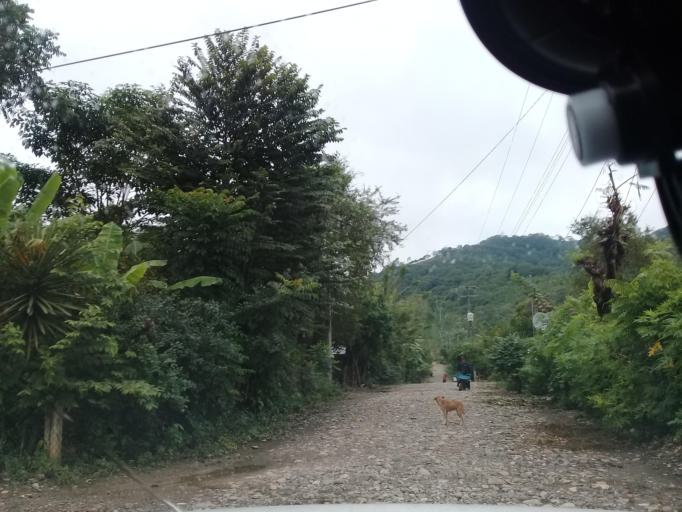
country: MX
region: Veracruz
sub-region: Chalma
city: San Pedro Coyutla
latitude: 21.2242
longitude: -98.4303
